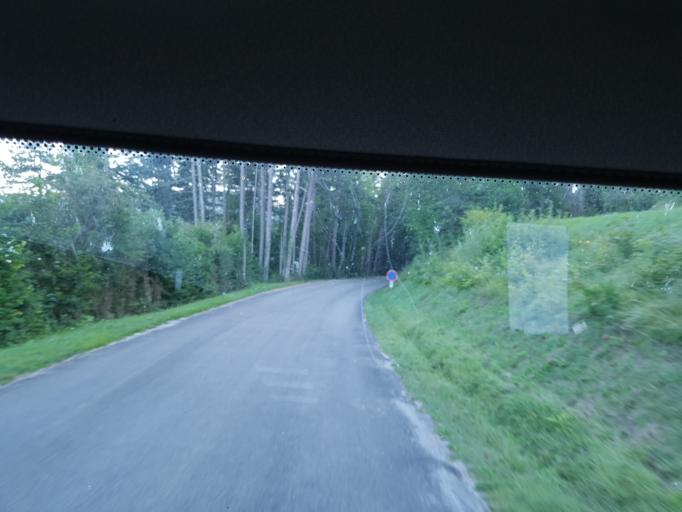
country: FR
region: Franche-Comte
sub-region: Departement du Jura
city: Orgelet
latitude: 46.4833
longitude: 5.6693
